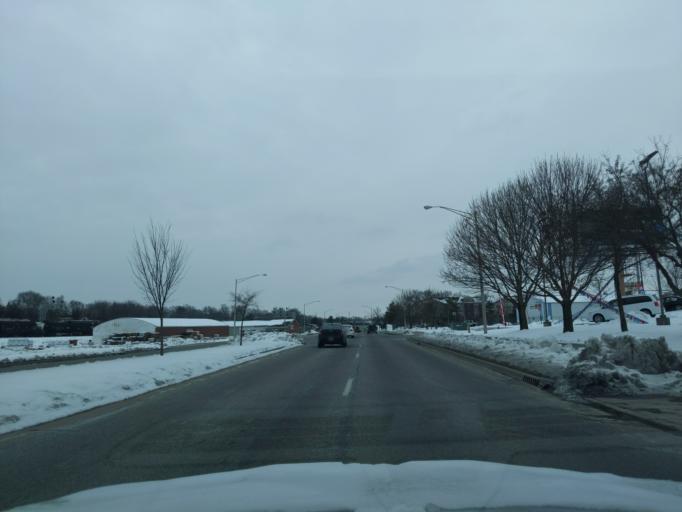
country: US
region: Indiana
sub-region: Tippecanoe County
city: Lafayette
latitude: 40.4373
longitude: -86.8859
